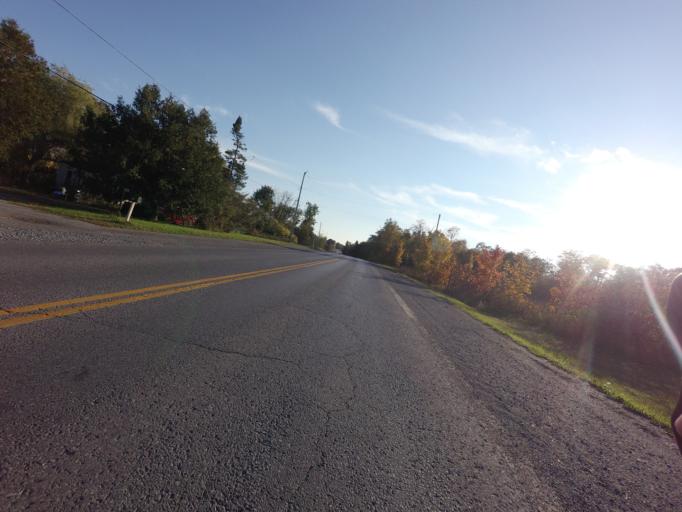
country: CA
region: Ontario
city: Kingston
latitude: 44.3377
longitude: -76.4540
